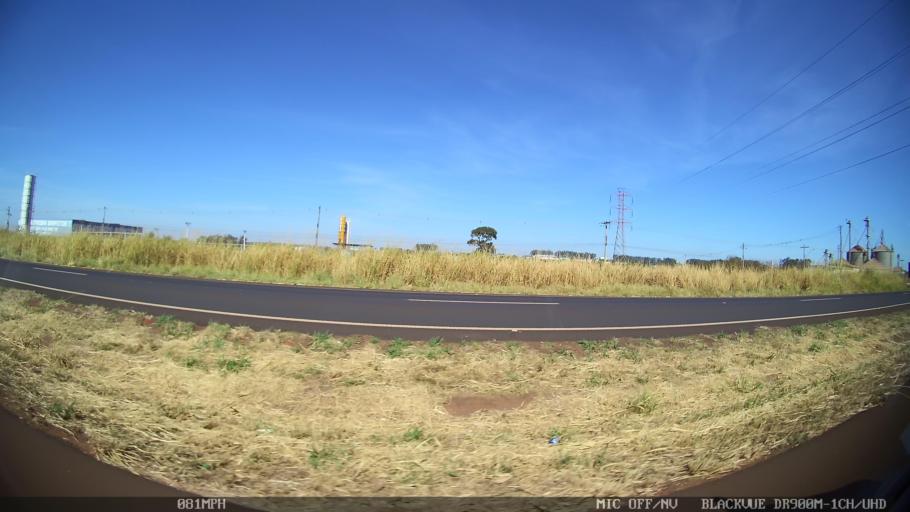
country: BR
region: Sao Paulo
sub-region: Barretos
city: Barretos
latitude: -20.5127
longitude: -48.5633
